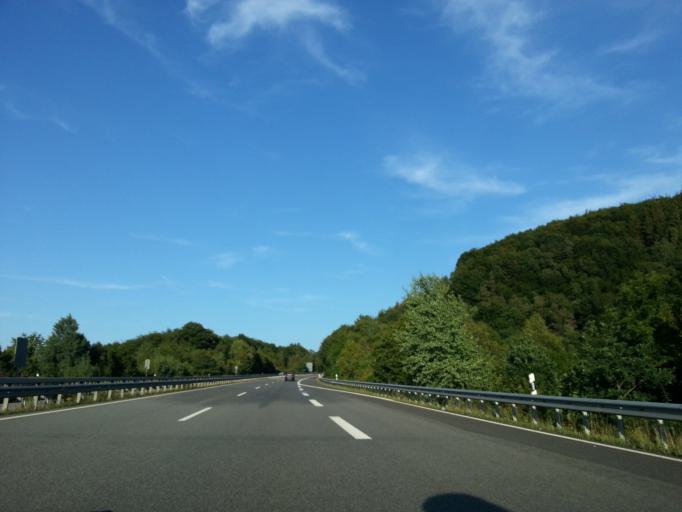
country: DE
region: Rheinland-Pfalz
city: Ellweiler
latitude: 49.6019
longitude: 7.1737
